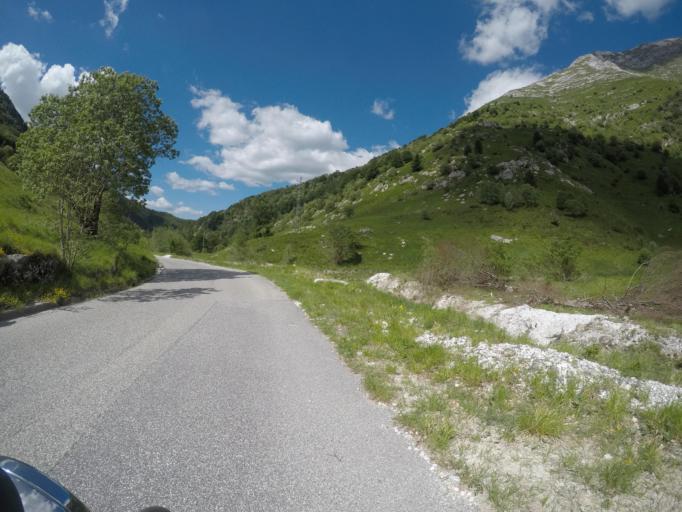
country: IT
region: Tuscany
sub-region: Provincia di Lucca
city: Minucciano
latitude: 44.1357
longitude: 10.1969
